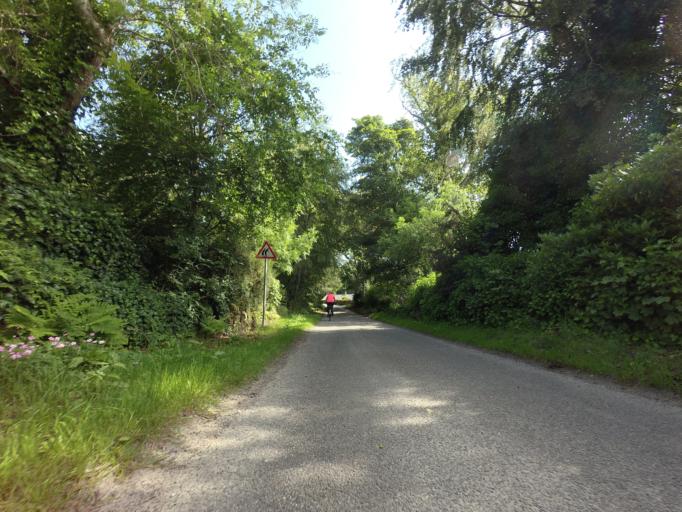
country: GB
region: Scotland
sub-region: Highland
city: Alness
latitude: 57.7179
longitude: -4.2155
